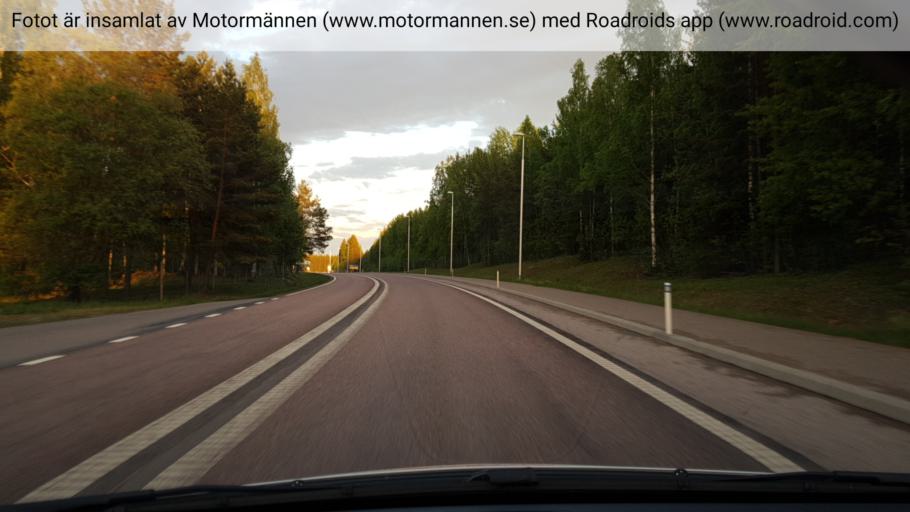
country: SE
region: Vaestmanland
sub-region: Fagersta Kommun
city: Fagersta
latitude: 59.9802
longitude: 15.8162
